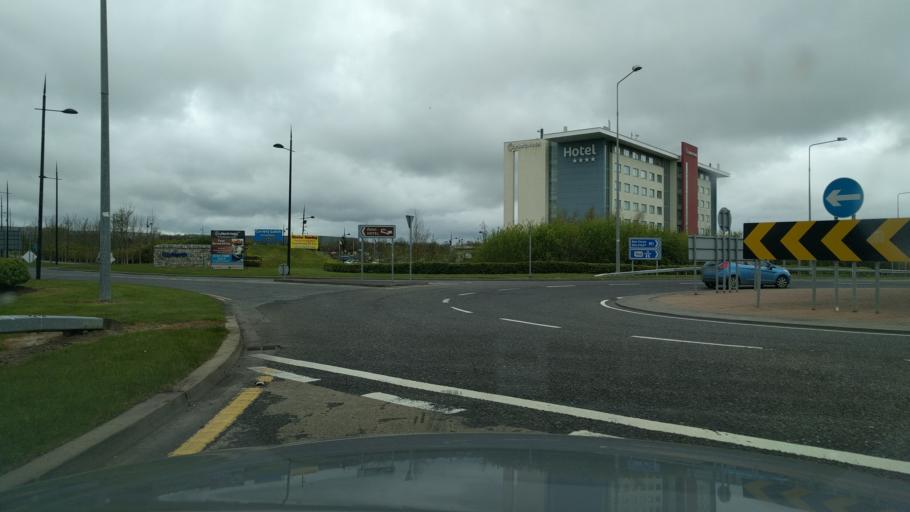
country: IE
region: Leinster
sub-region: An Mhi
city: Stamullin
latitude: 53.6381
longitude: -6.2557
